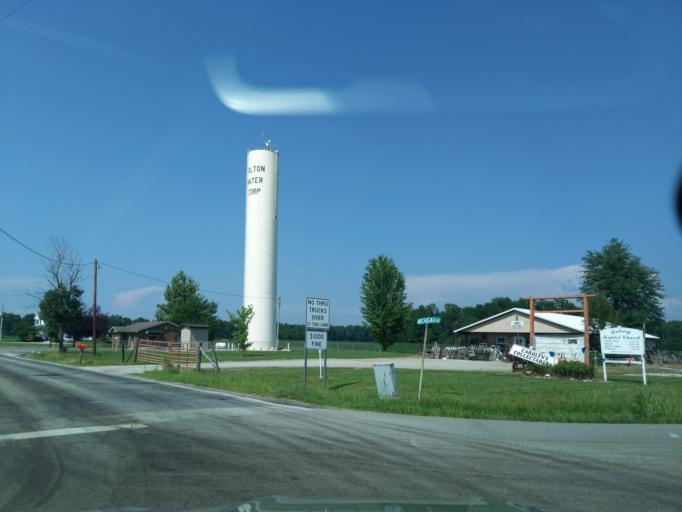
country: US
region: Indiana
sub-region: Ripley County
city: Osgood
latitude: 39.0751
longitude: -85.3488
